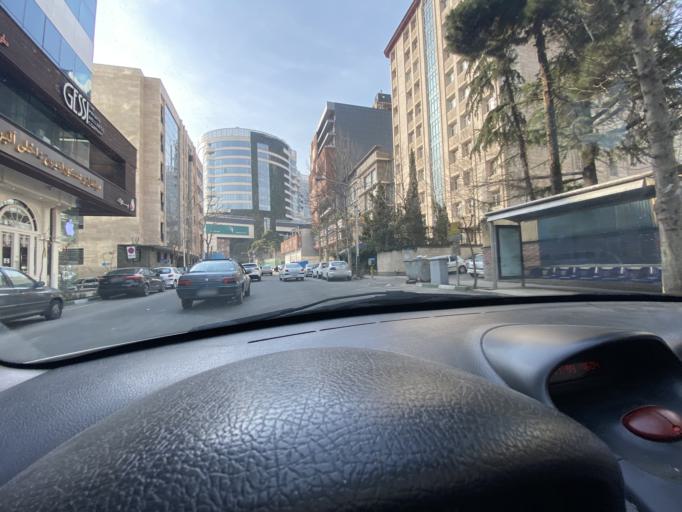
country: IR
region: Tehran
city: Tajrish
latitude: 35.8058
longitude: 51.4738
